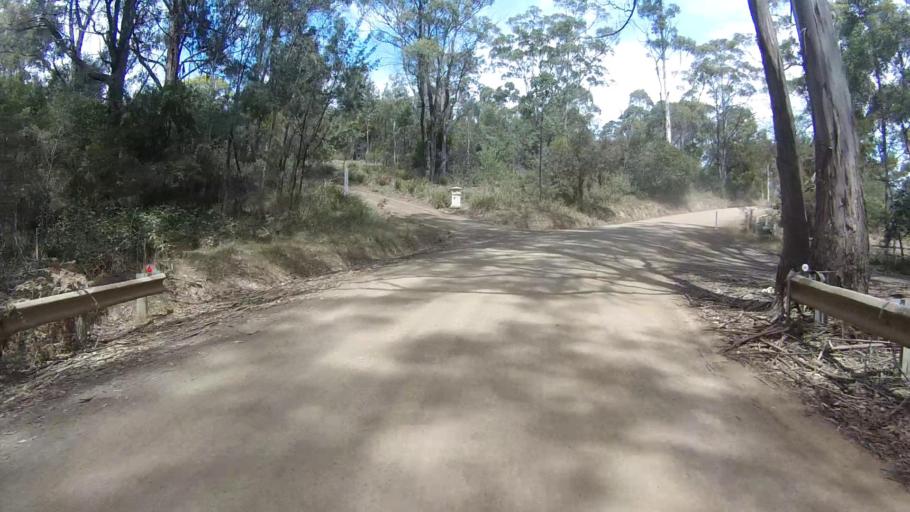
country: AU
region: Tasmania
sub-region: Kingborough
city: Blackmans Bay
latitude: -43.0458
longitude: 147.3078
